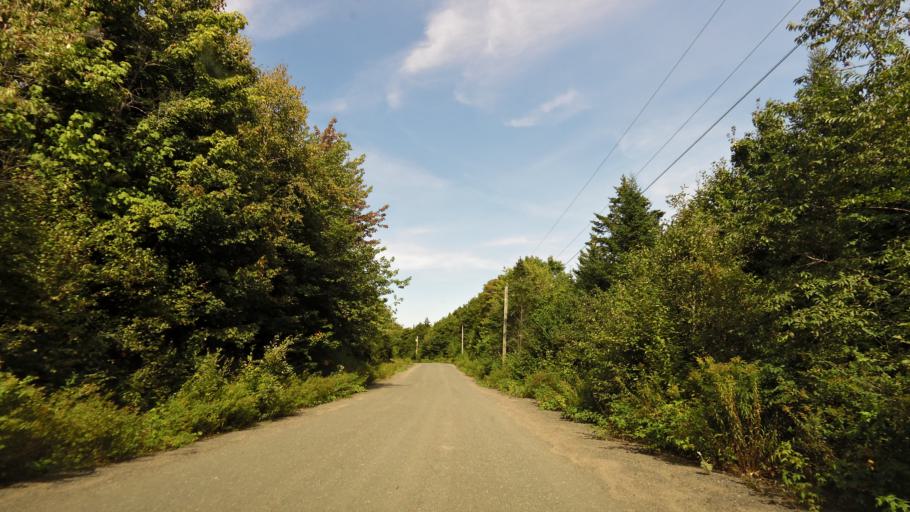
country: CA
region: New Brunswick
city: Hampton
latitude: 45.5719
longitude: -65.8321
